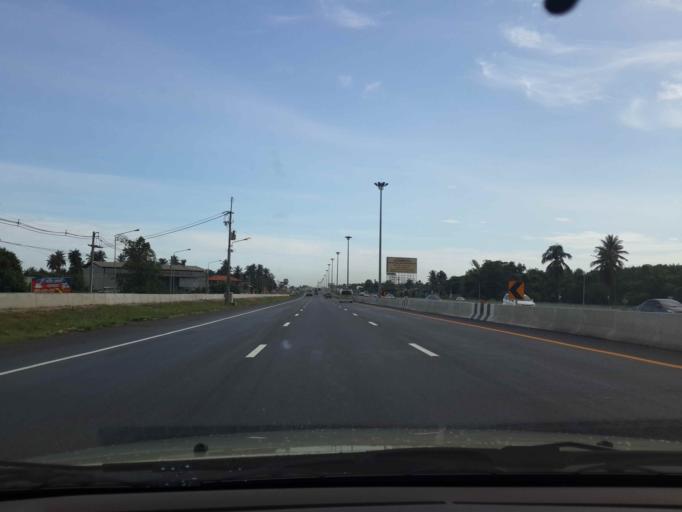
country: TH
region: Chon Buri
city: Ban Talat Bueng
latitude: 13.0142
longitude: 100.9964
